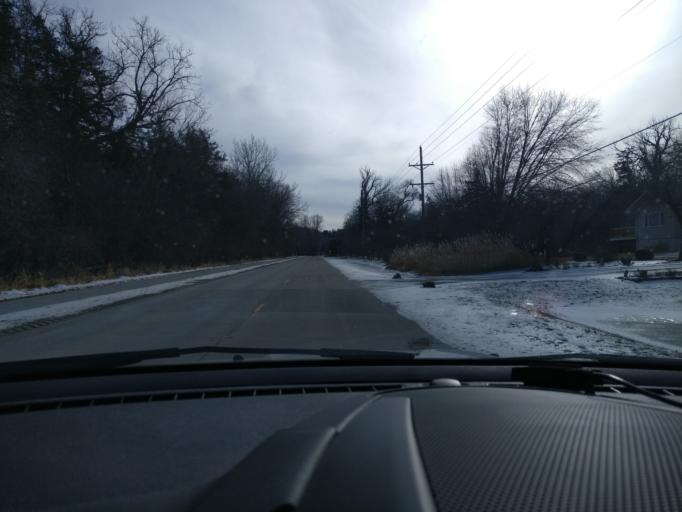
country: US
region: Nebraska
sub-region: Dodge County
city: Fremont
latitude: 41.4166
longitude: -96.5216
